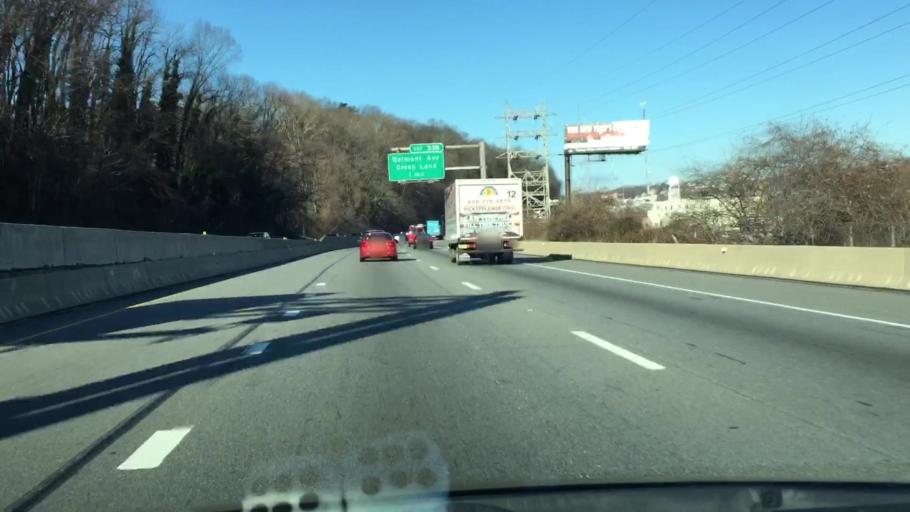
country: US
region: Pennsylvania
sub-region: Montgomery County
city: Bala-Cynwyd
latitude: 40.0140
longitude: -75.2132
